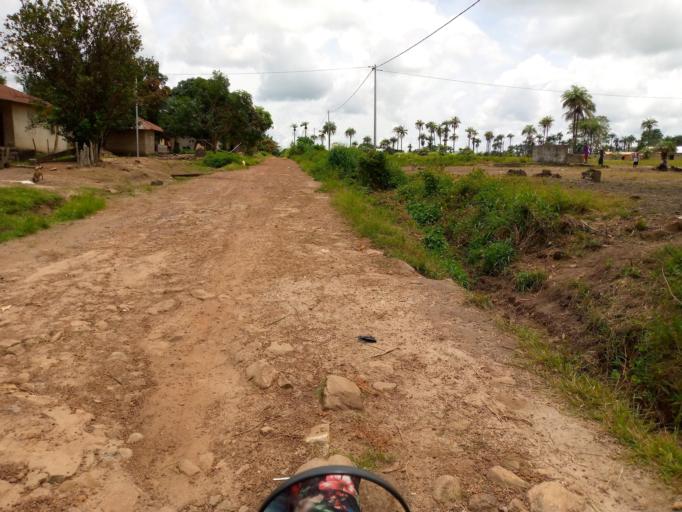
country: SL
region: Northern Province
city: Binkolo
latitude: 9.1107
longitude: -12.1991
